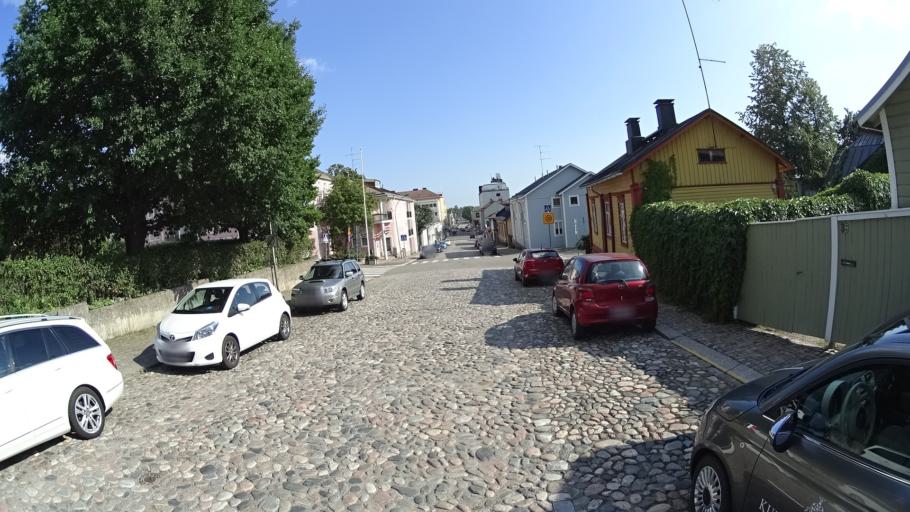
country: FI
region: Uusimaa
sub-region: Porvoo
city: Porvoo
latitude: 60.3963
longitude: 25.6624
